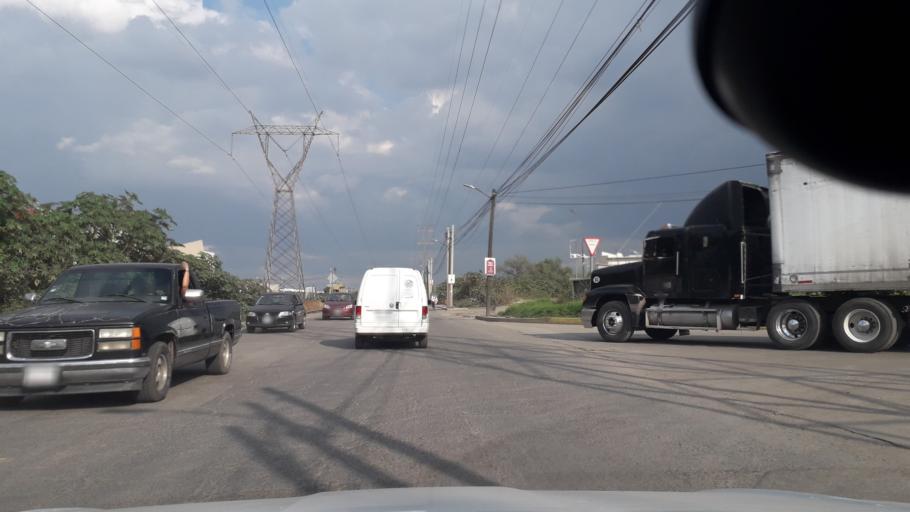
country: MX
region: Mexico
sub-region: Tultitlan
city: Colonia Lazaro Cardenas (Los Hornos)
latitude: 19.6394
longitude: -99.1506
